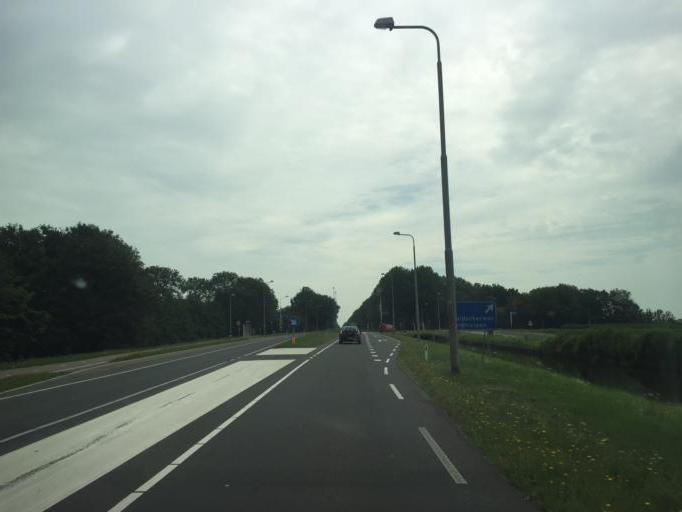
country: NL
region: North Holland
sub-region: Gemeente Alkmaar
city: Alkmaar
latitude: 52.6170
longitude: 4.7950
